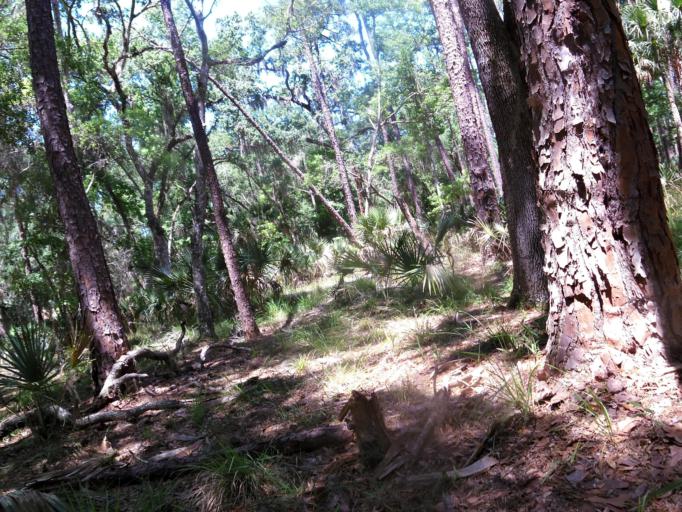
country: US
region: Florida
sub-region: Flagler County
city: Flagler Beach
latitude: 29.4354
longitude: -81.1398
